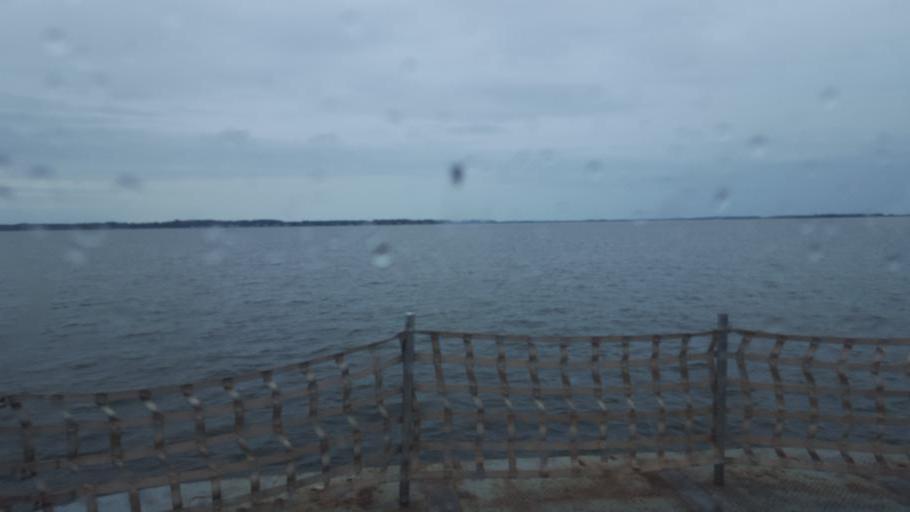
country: US
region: North Carolina
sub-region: Currituck County
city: Currituck
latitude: 36.4715
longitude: -75.9517
